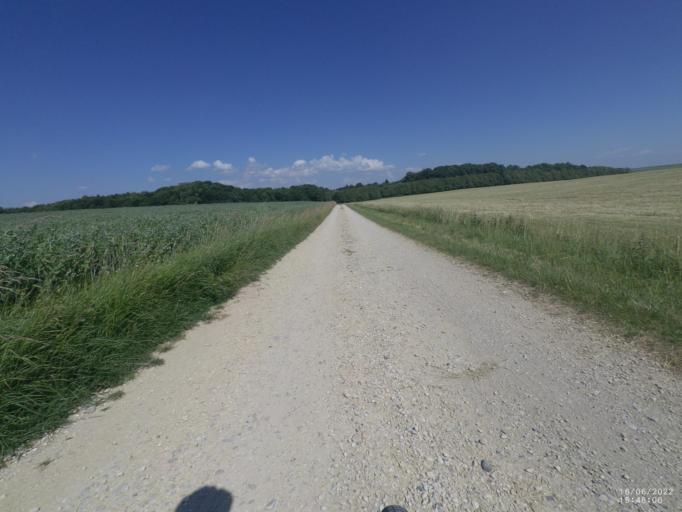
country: DE
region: Baden-Wuerttemberg
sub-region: Regierungsbezirk Stuttgart
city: Gerstetten
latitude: 48.6140
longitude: 10.0785
